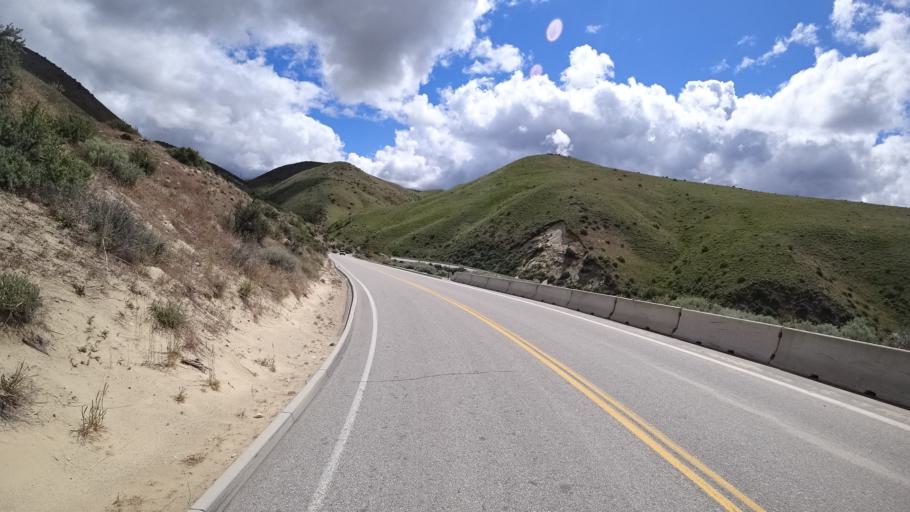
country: US
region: Idaho
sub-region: Ada County
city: Boise
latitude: 43.6823
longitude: -116.1818
